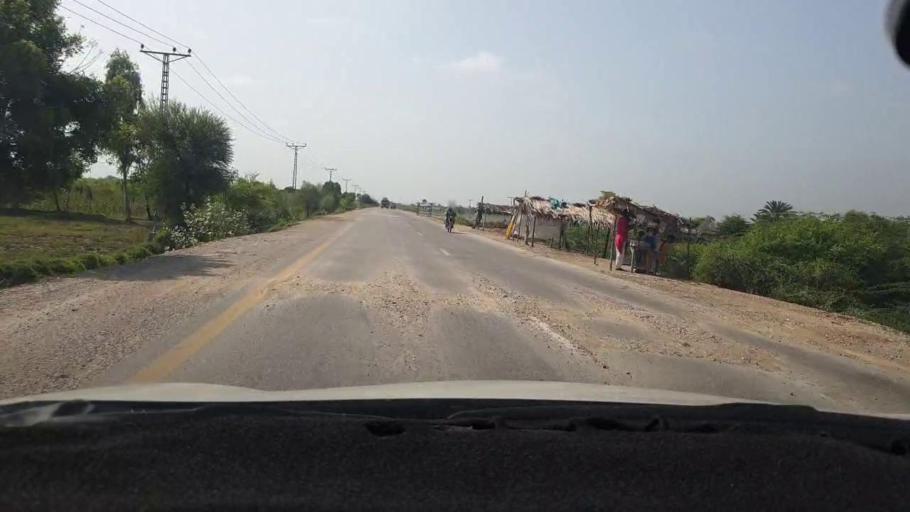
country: PK
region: Sindh
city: Tando Mittha Khan
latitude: 25.7844
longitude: 69.0713
